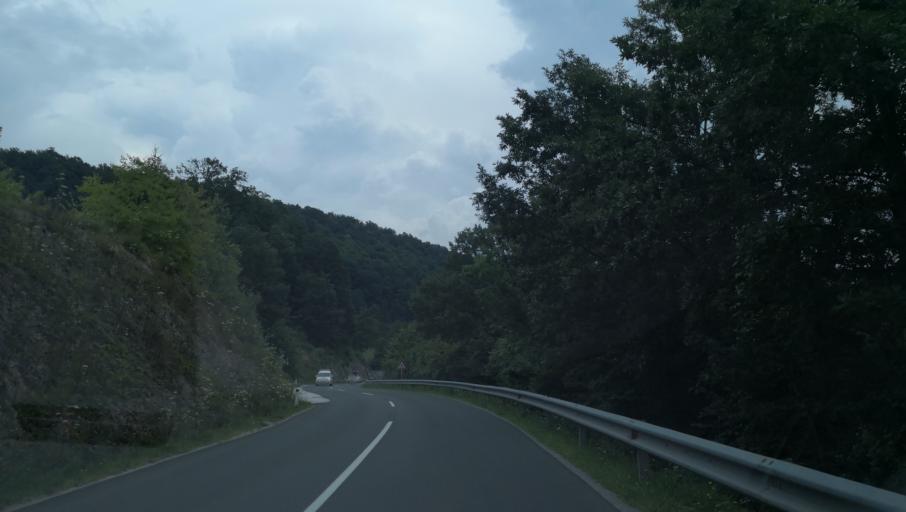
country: SI
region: Zuzemberk
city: Zuzemberk
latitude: 45.8289
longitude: 14.9377
